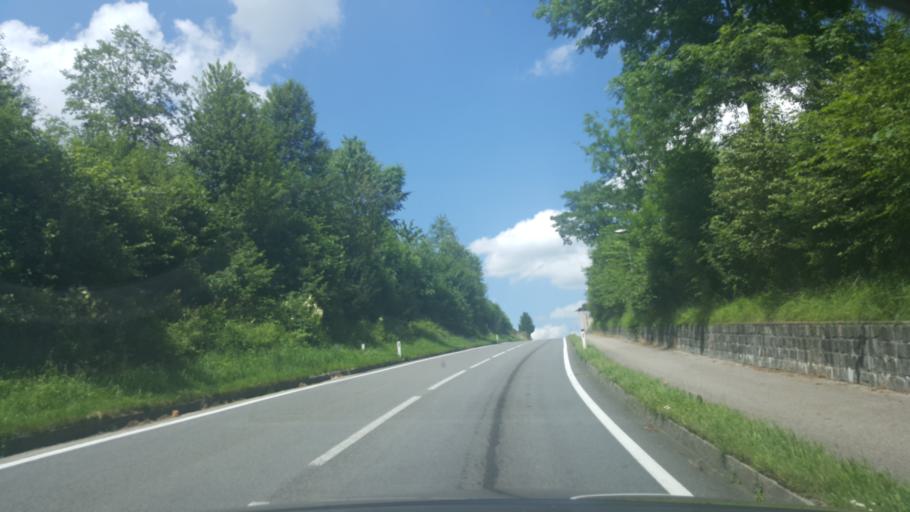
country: AT
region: Upper Austria
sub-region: Politischer Bezirk Vocklabruck
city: Gampern
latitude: 47.9987
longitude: 13.5449
